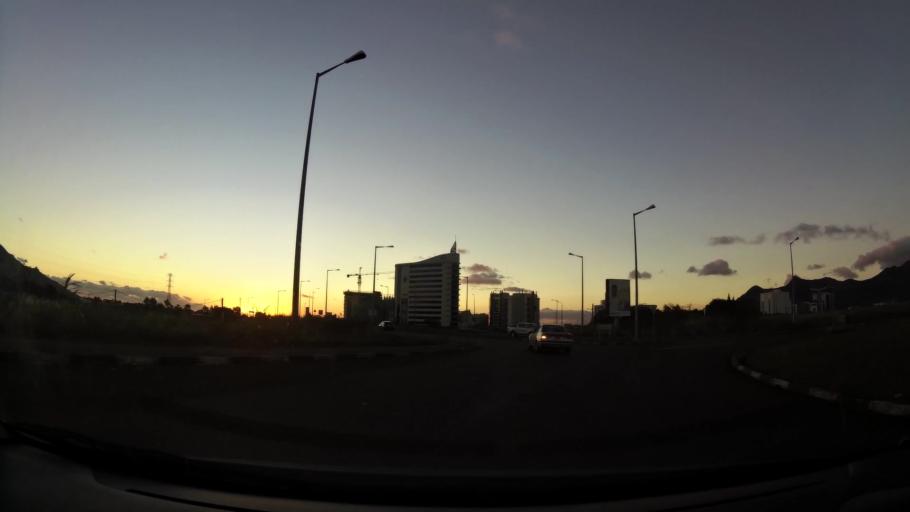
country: MU
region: Plaines Wilhems
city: Ebene
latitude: -20.2503
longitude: 57.4952
